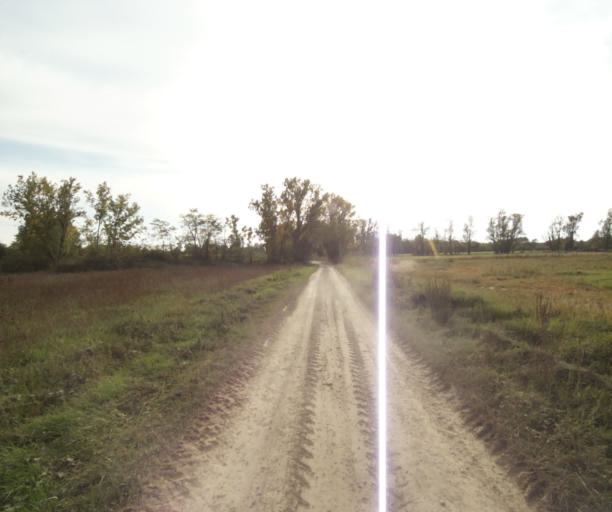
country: FR
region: Midi-Pyrenees
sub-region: Departement du Tarn-et-Garonne
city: Campsas
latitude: 43.9045
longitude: 1.3160
